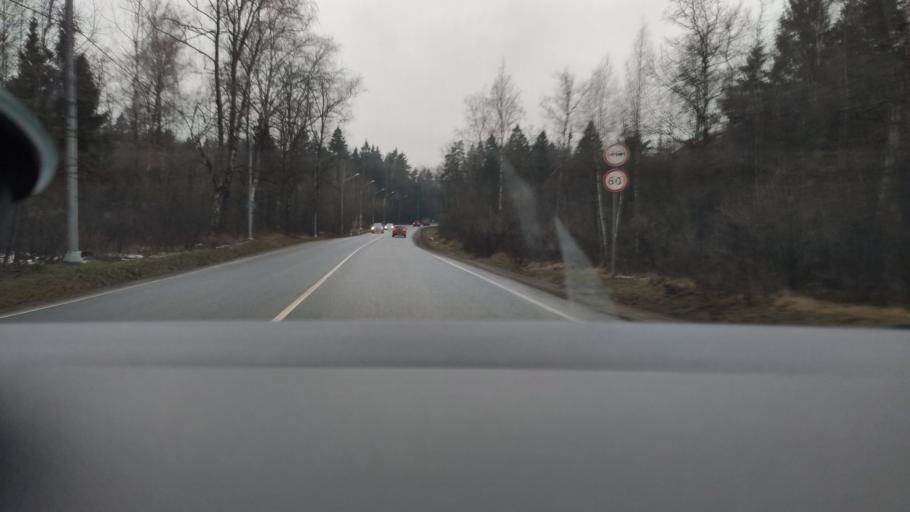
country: RU
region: Moskovskaya
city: Gorki Vtoryye
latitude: 55.6985
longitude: 37.1232
